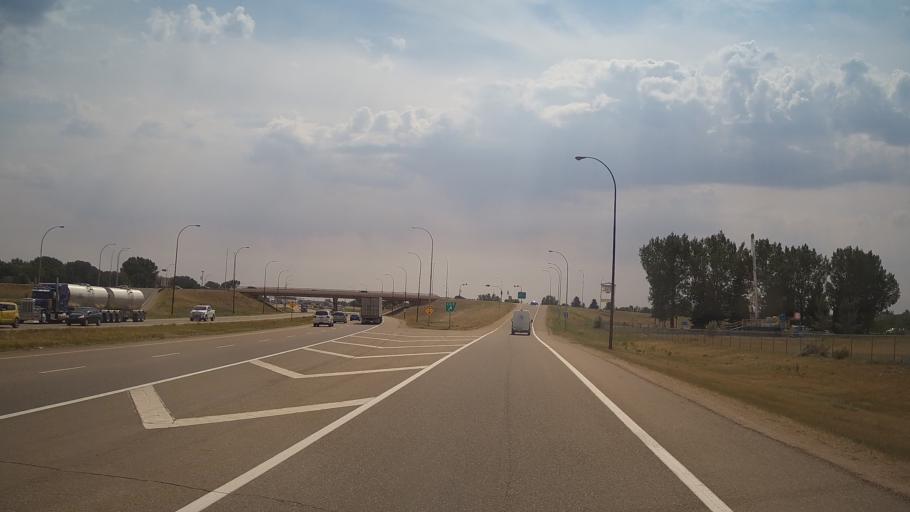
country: CA
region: Alberta
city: Medicine Hat
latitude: 50.0137
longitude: -110.6862
